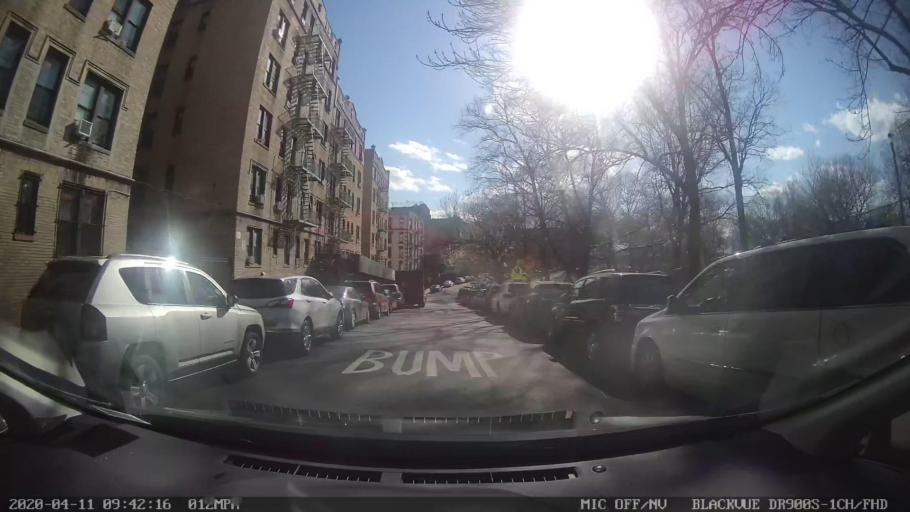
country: US
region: New York
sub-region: Bronx
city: The Bronx
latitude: 40.8373
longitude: -73.8897
